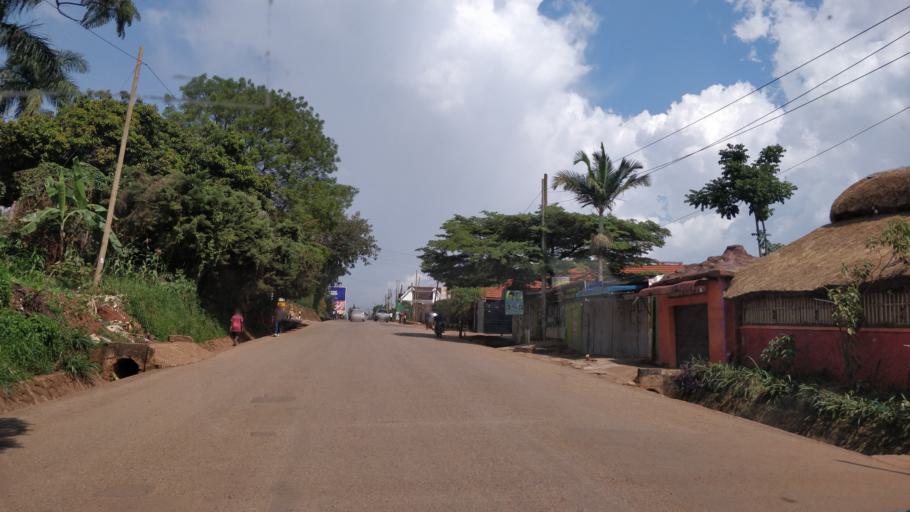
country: UG
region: Central Region
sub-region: Kampala District
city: Kampala
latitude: 0.2994
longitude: 32.6049
